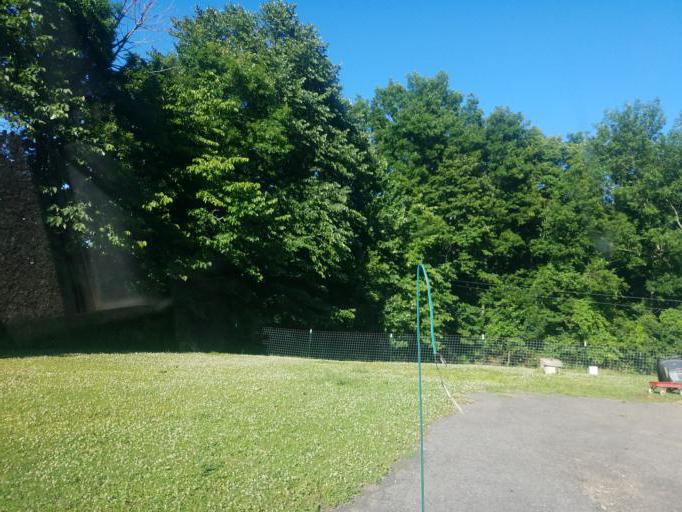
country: US
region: New York
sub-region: Wayne County
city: Lyons
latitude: 43.0996
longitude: -77.0092
